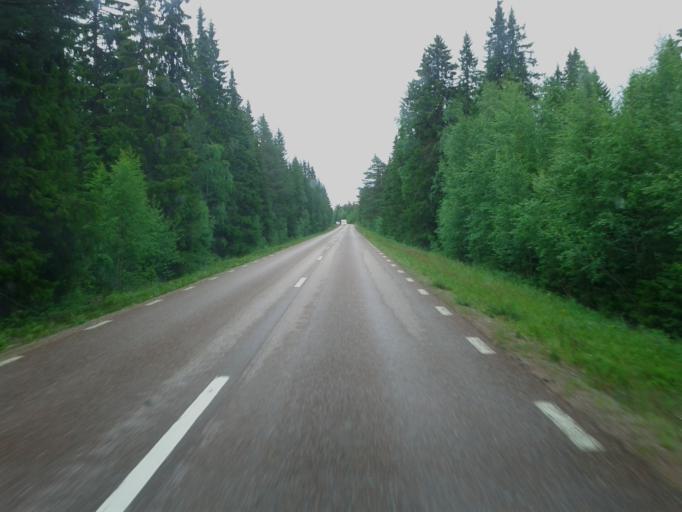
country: NO
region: Hedmark
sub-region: Trysil
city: Innbygda
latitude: 61.8309
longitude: 12.8467
